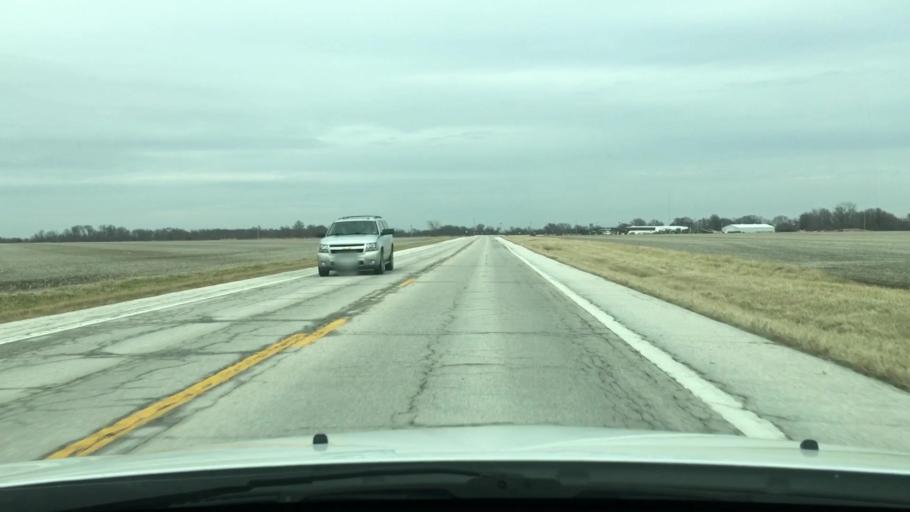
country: US
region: Missouri
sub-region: Audrain County
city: Vandalia
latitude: 39.3414
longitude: -91.4180
